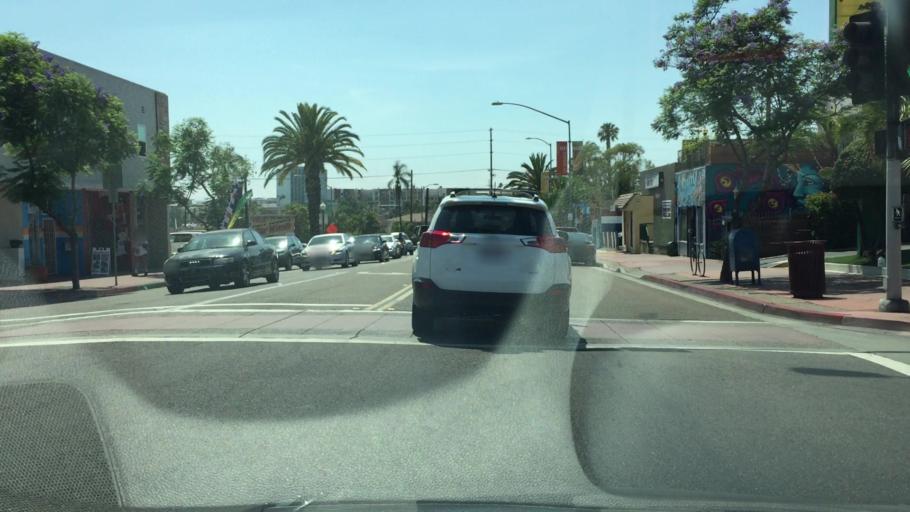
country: US
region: California
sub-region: San Diego County
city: San Diego
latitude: 32.7498
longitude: -117.1194
